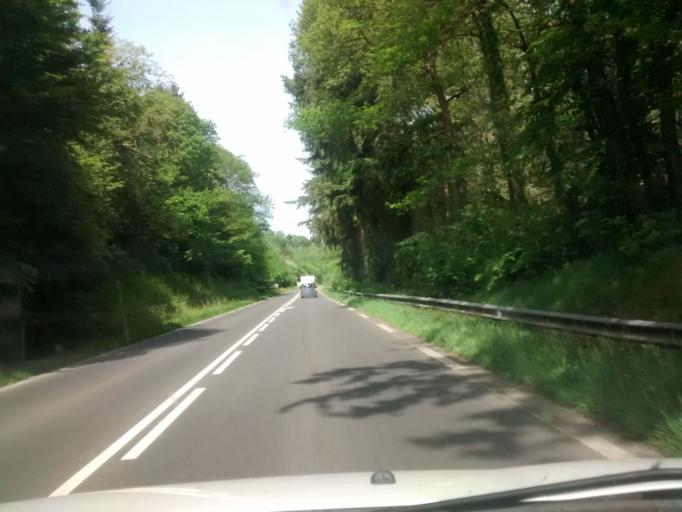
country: FR
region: Brittany
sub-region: Departement d'Ille-et-Vilaine
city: Antrain
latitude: 48.4607
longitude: -1.5000
